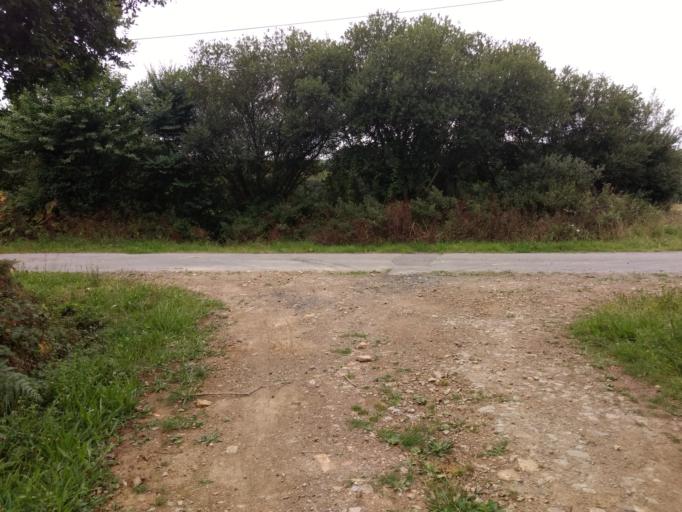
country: FR
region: Brittany
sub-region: Departement du Finistere
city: Loperhet
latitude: 48.3579
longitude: -4.2942
